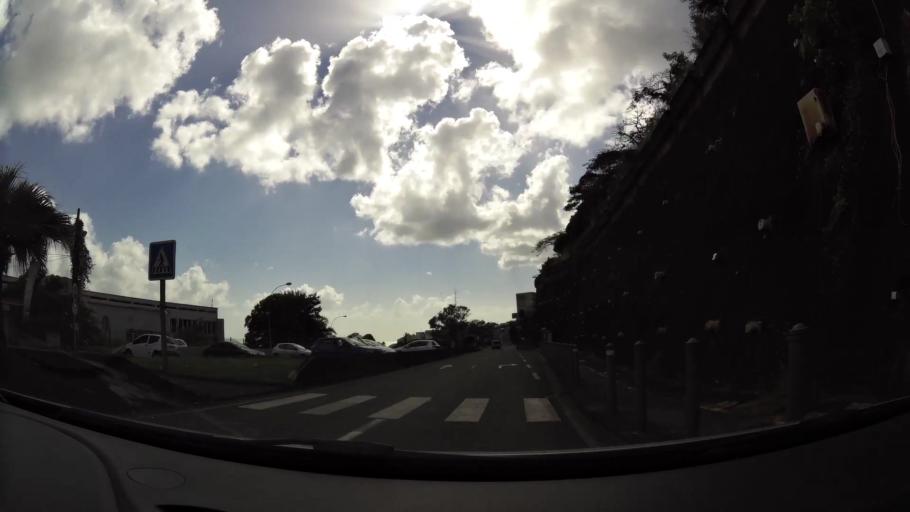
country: MQ
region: Martinique
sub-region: Martinique
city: Fort-de-France
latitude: 14.6150
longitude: -61.0623
